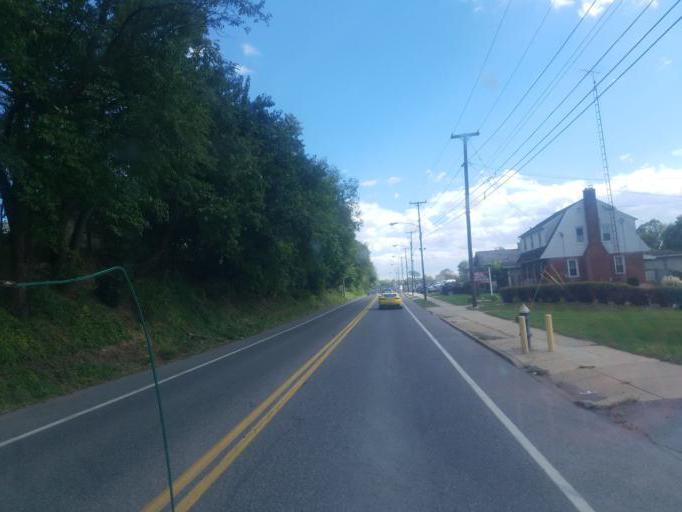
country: US
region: Pennsylvania
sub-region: Franklin County
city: Chambersburg
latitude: 39.9364
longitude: -77.6713
